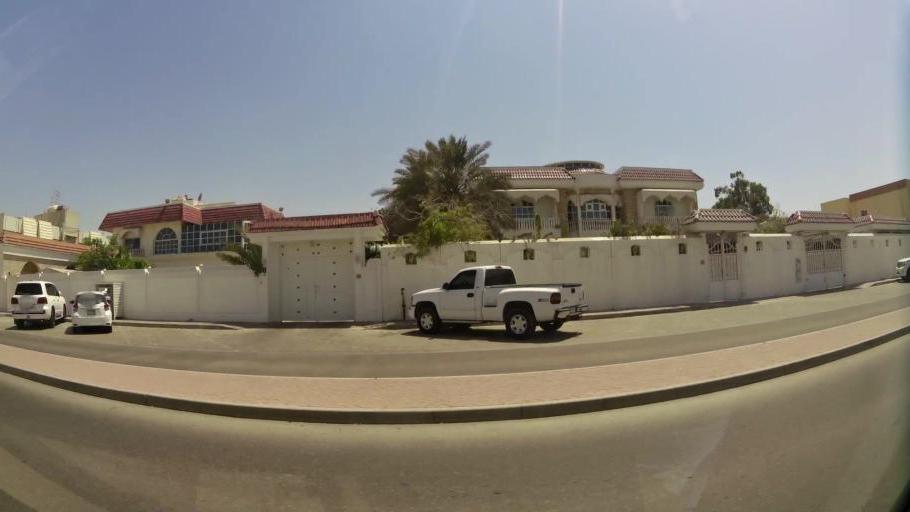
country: AE
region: Ash Shariqah
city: Sharjah
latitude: 25.2879
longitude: 55.3450
